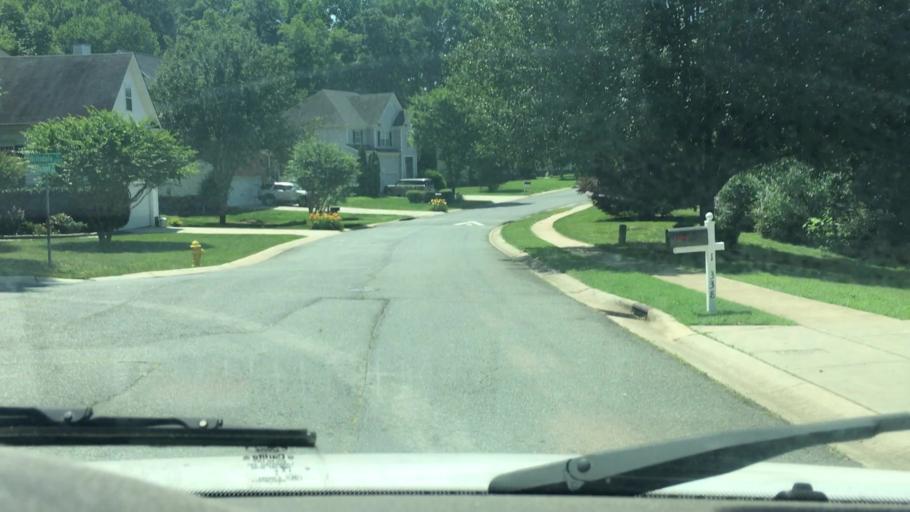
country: US
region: North Carolina
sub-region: Mecklenburg County
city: Huntersville
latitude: 35.4456
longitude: -80.8509
